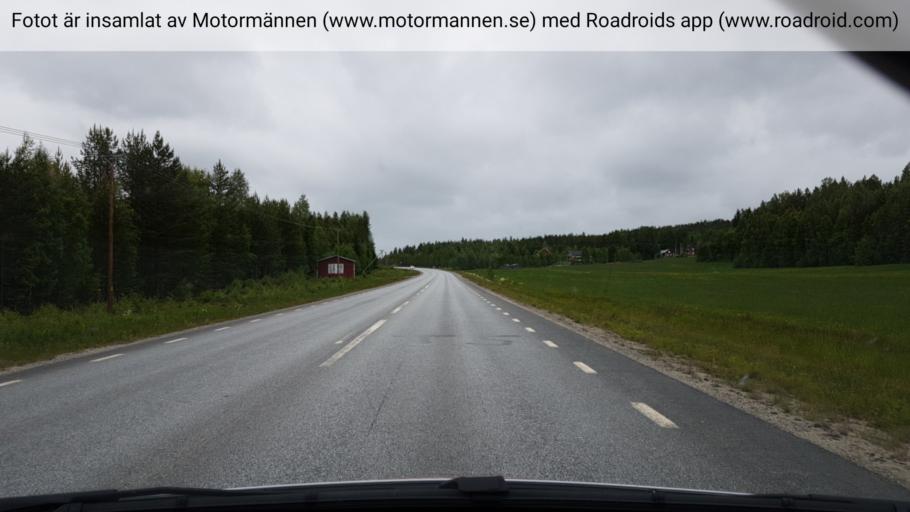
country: SE
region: Vaesterbotten
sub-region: Vannas Kommun
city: Vaennaes
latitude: 64.0255
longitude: 19.6926
